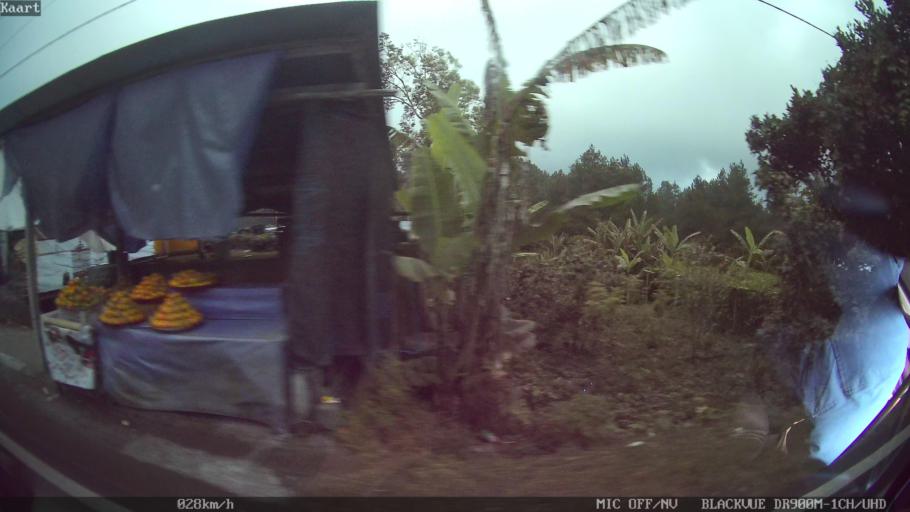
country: ID
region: Bali
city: Banjar Kedisan
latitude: -8.2715
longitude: 115.3305
